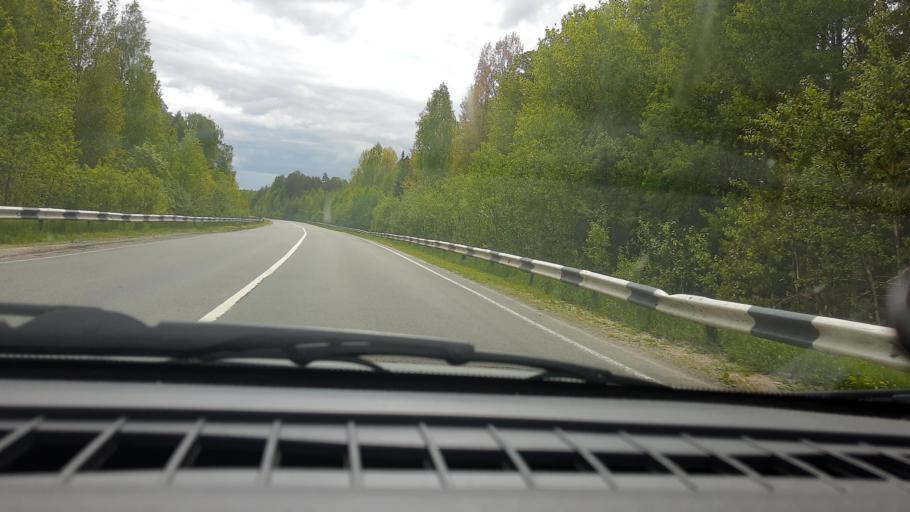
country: RU
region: Nizjnij Novgorod
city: Semenov
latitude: 56.8041
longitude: 44.4618
